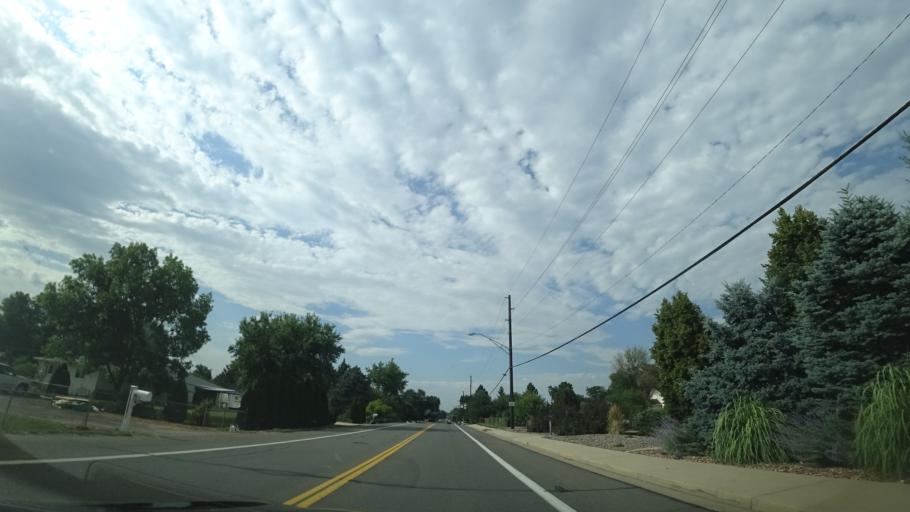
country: US
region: Colorado
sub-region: Jefferson County
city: Lakewood
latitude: 39.7159
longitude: -105.1002
